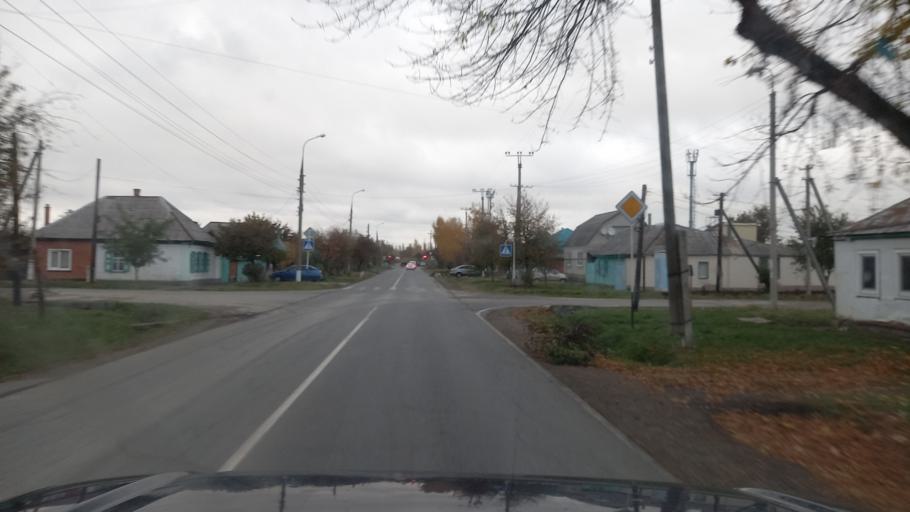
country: RU
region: Adygeya
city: Maykop
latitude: 44.6135
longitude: 40.1276
